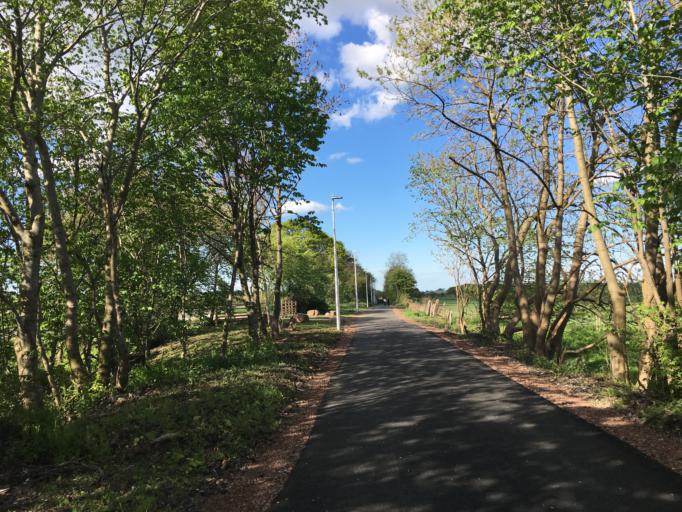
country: GB
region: Scotland
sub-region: Midlothian
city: Loanhead
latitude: 55.8952
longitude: -3.1324
